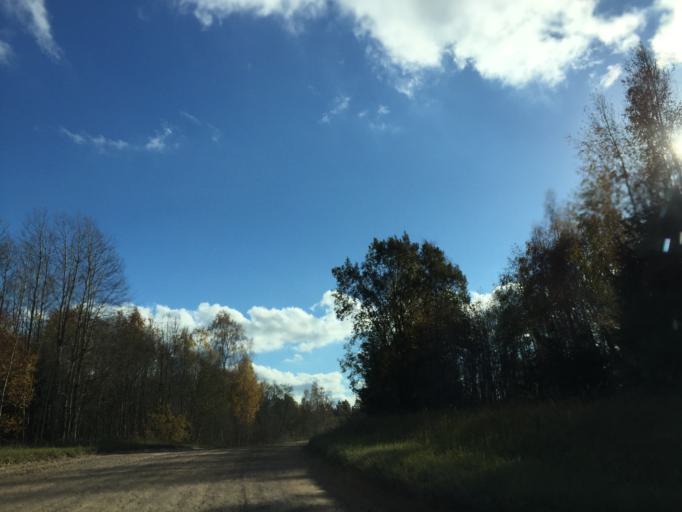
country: LV
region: Tukuma Rajons
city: Tukums
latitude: 56.9619
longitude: 22.9775
